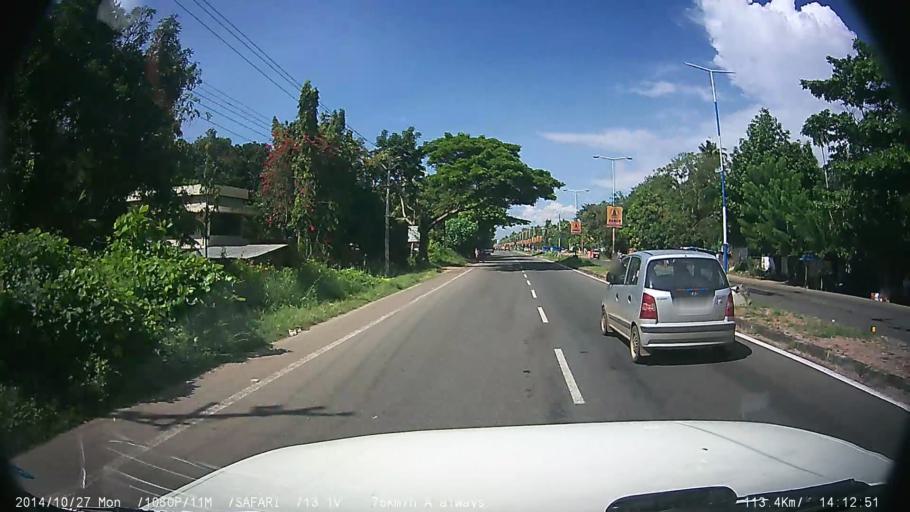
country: IN
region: Kerala
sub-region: Alappuzha
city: Kutiatodu
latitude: 9.8067
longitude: 76.3140
